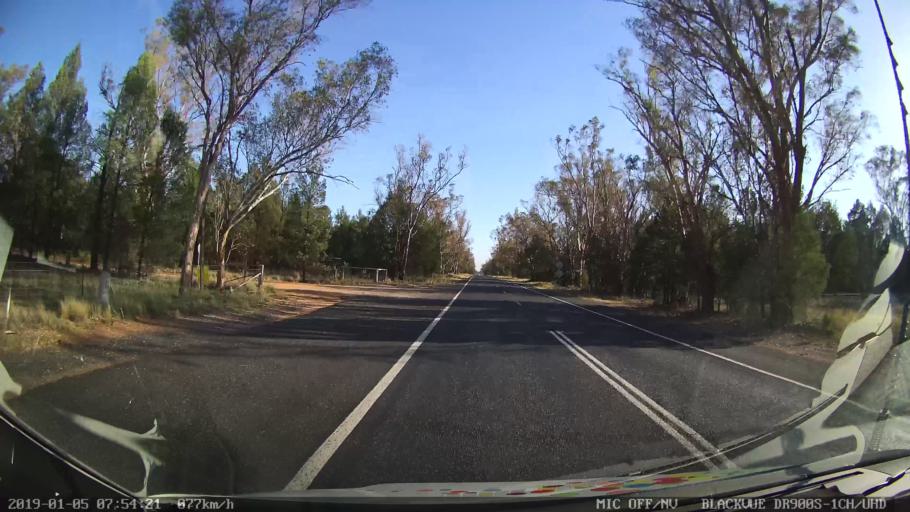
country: AU
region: New South Wales
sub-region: Gilgandra
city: Gilgandra
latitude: -31.7341
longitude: 148.6486
